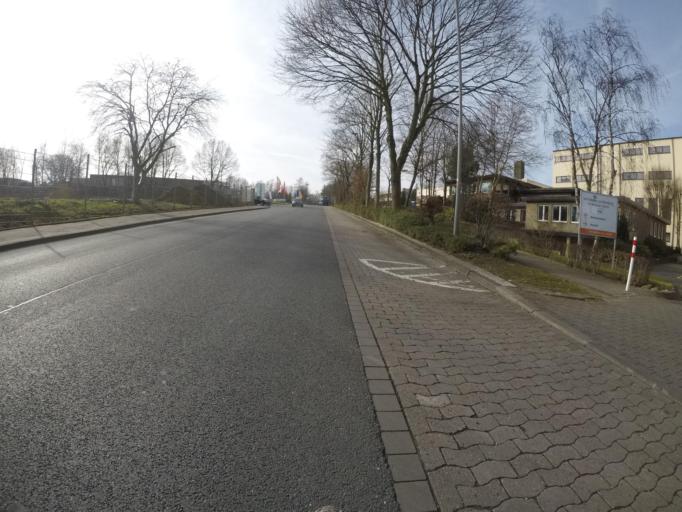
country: DE
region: North Rhine-Westphalia
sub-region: Regierungsbezirk Detmold
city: Herford
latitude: 52.1314
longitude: 8.6423
